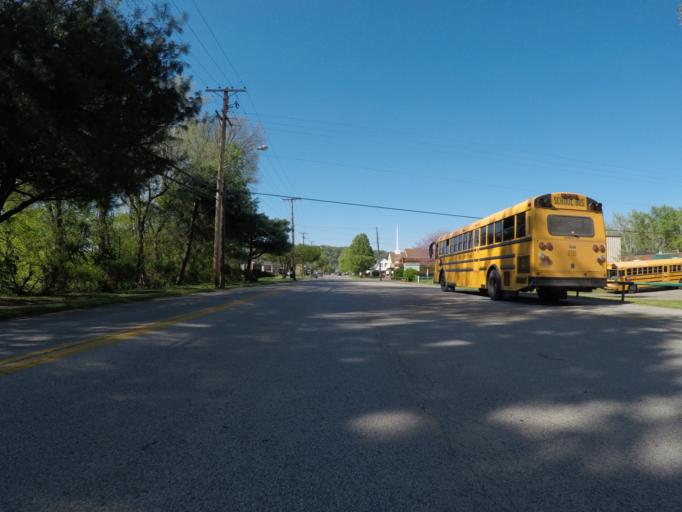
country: US
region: West Virginia
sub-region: Wayne County
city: Ceredo
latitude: 38.3935
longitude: -82.5593
